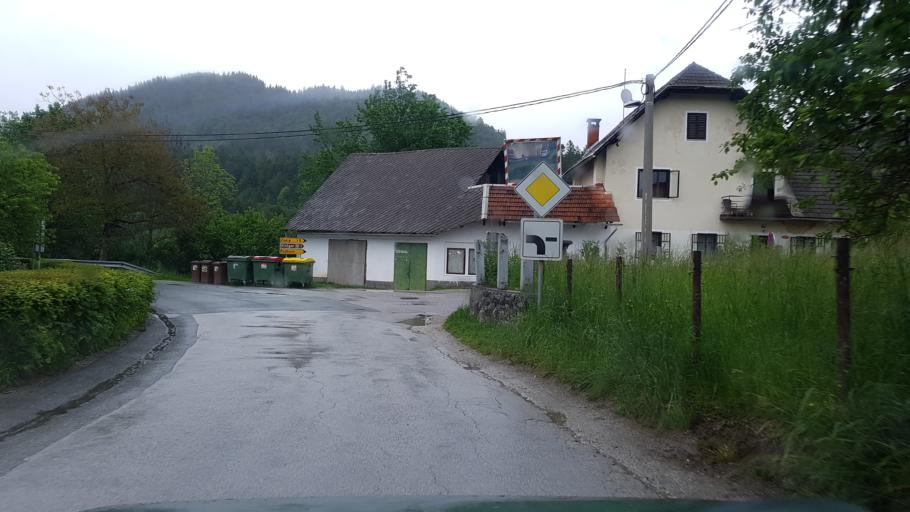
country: SI
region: Gorje
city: Zgornje Gorje
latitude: 46.3877
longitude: 14.0782
